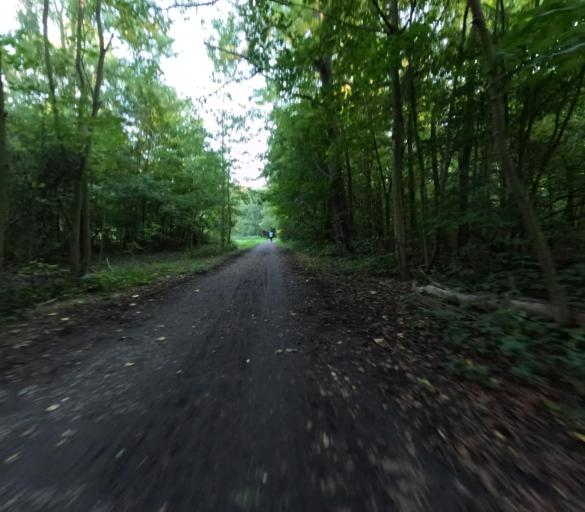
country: DE
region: Saxony
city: Leipzig
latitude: 51.3602
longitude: 12.3232
